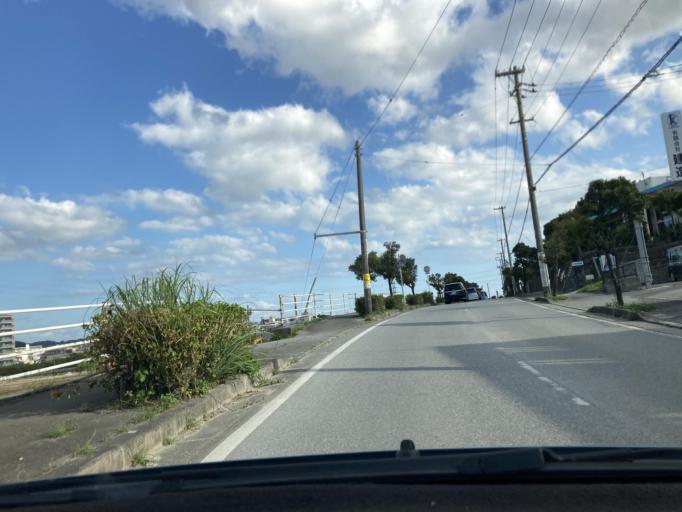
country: JP
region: Okinawa
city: Tomigusuku
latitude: 26.1892
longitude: 127.7058
